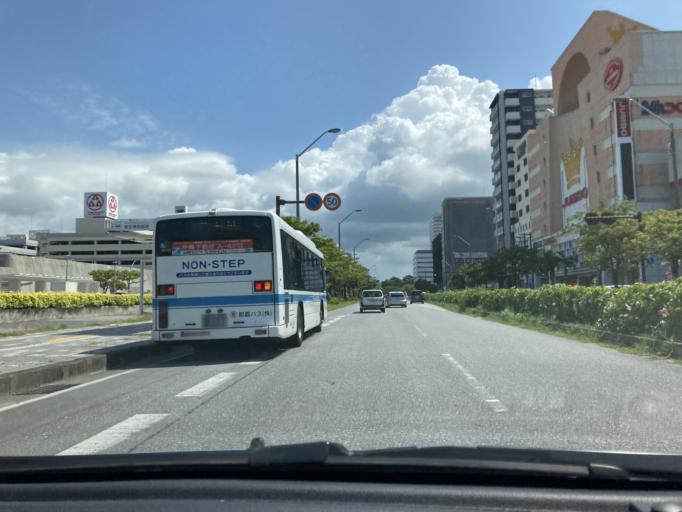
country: JP
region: Okinawa
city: Naha-shi
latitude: 26.2270
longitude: 127.6925
